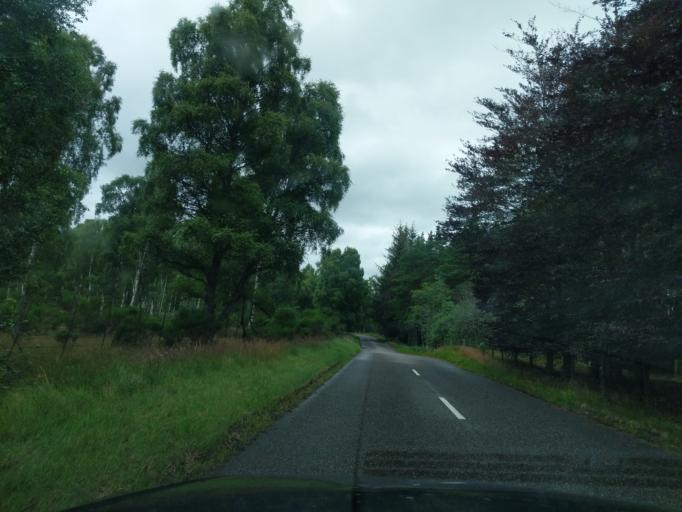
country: GB
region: Scotland
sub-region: Aberdeenshire
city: Aboyne
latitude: 57.0676
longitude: -2.8197
